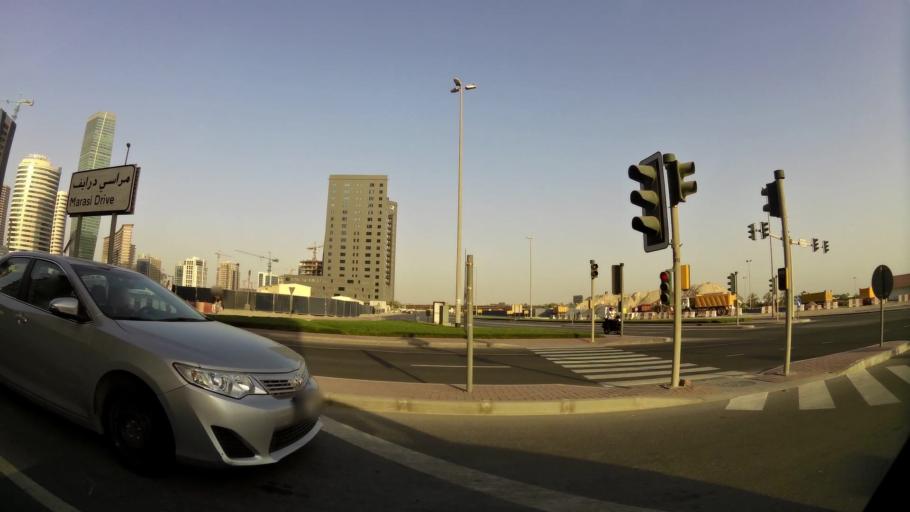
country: AE
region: Dubai
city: Dubai
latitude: 25.1795
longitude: 55.2641
